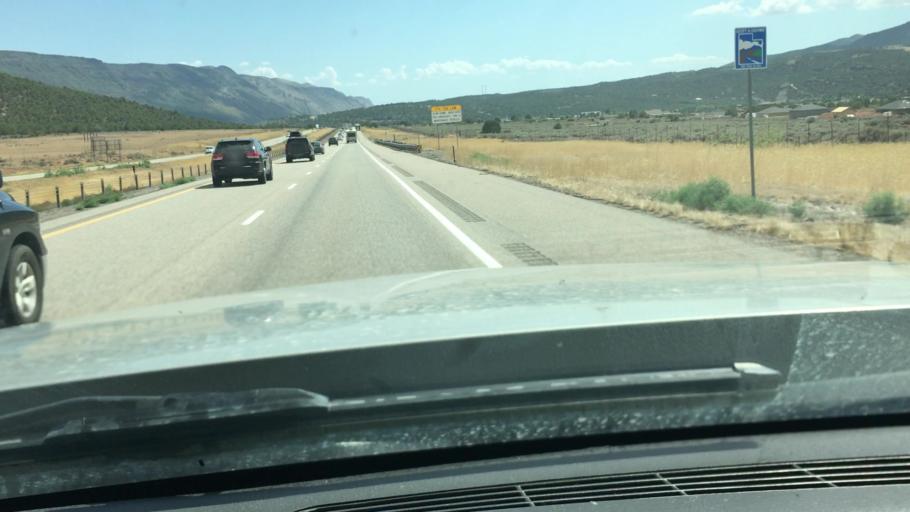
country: US
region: Utah
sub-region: Washington County
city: Toquerville
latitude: 37.4390
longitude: -113.2326
